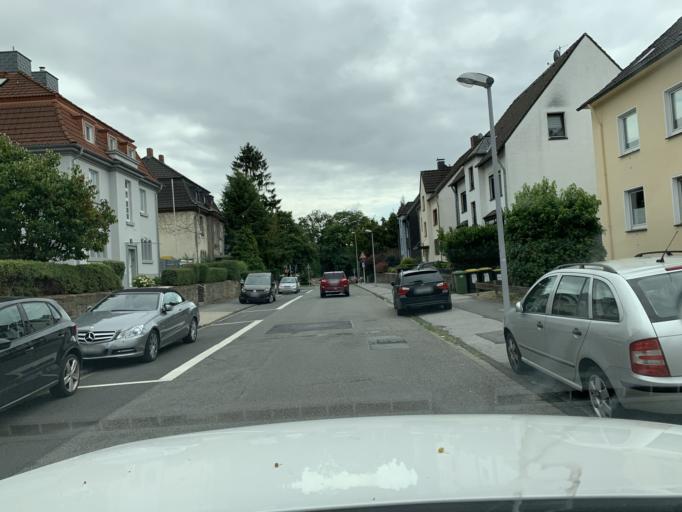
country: DE
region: North Rhine-Westphalia
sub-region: Regierungsbezirk Dusseldorf
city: Muelheim (Ruhr)
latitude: 51.4477
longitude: 6.9052
